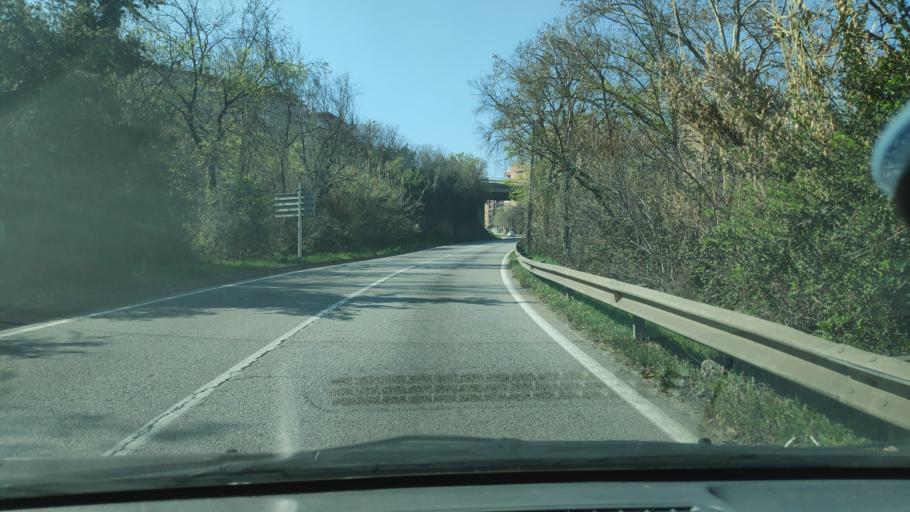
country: ES
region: Catalonia
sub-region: Provincia de Barcelona
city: Sabadell
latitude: 41.5333
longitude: 2.1218
